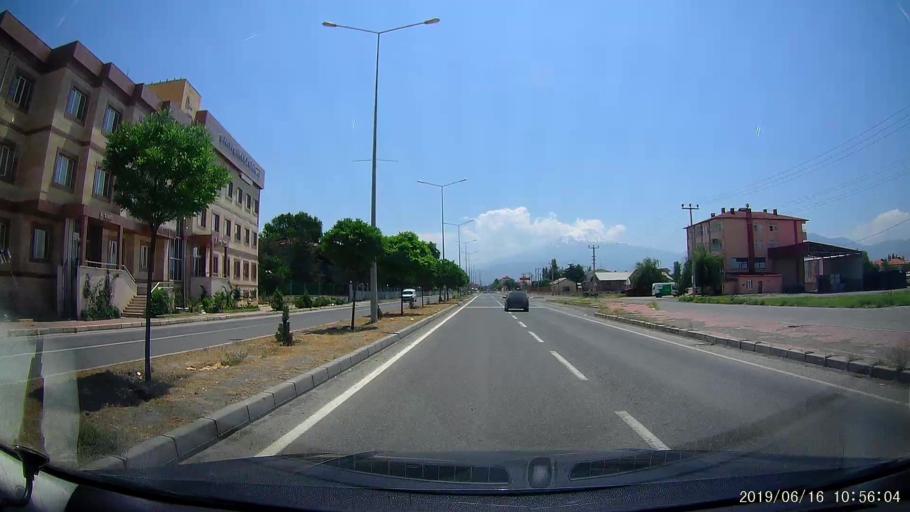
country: TR
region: Igdir
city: Igdir
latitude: 39.9326
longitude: 44.0174
